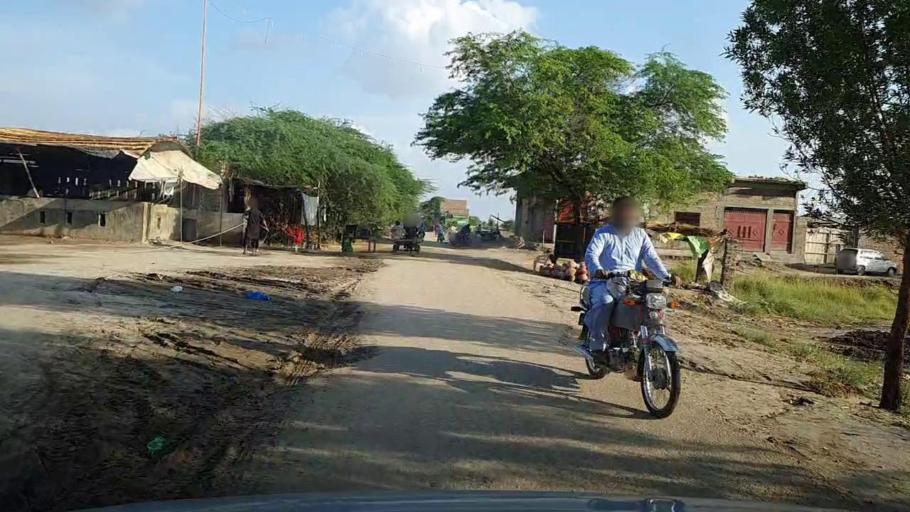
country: PK
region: Sindh
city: Hingorja
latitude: 27.0901
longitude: 68.4174
